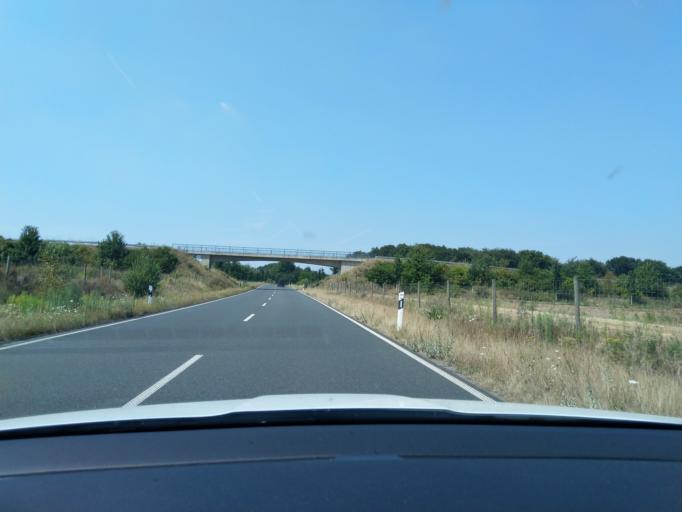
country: DE
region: North Rhine-Westphalia
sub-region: Regierungsbezirk Koln
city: Wassenberg
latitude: 51.1263
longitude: 6.1984
